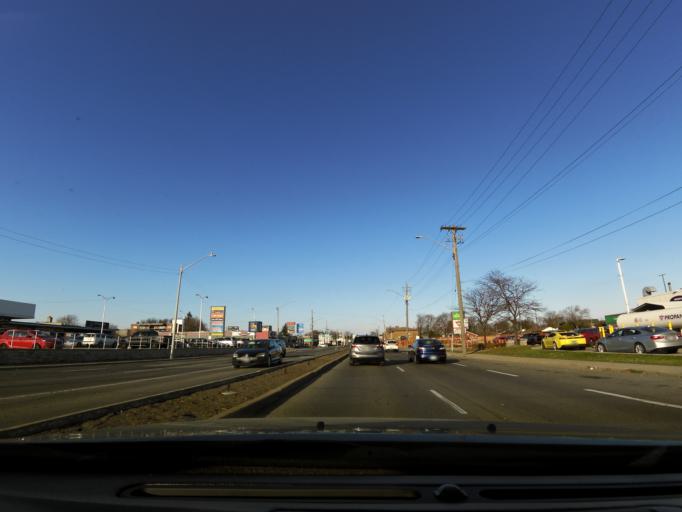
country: CA
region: Ontario
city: Hamilton
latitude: 43.2289
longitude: -79.8817
